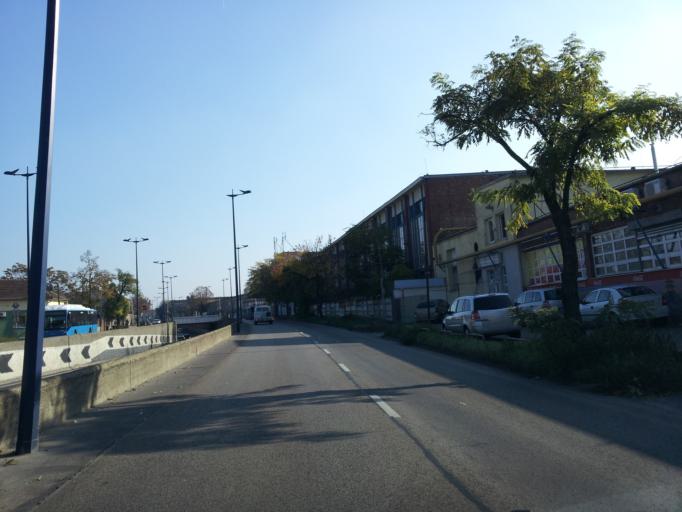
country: HU
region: Budapest
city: Budapest XVIII. keruelet
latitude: 47.4584
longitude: 19.1750
